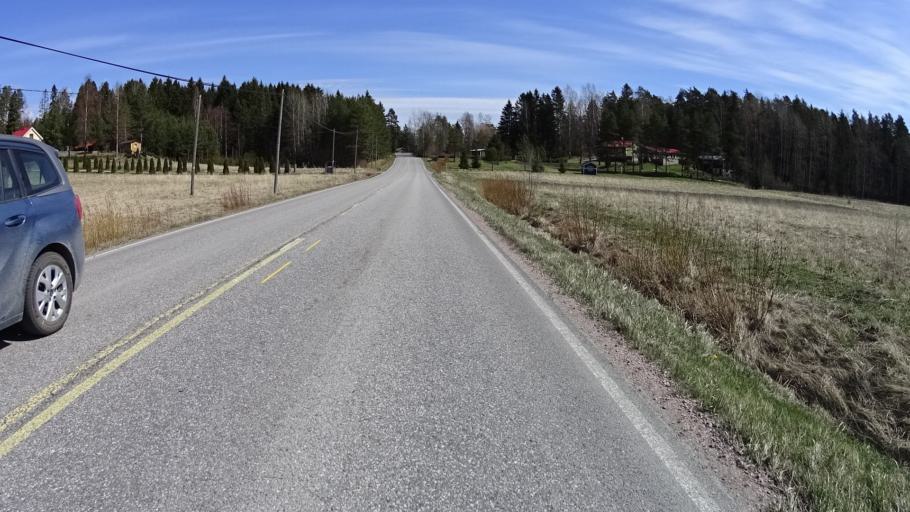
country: FI
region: Uusimaa
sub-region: Helsinki
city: Kirkkonummi
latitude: 60.1900
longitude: 24.4028
